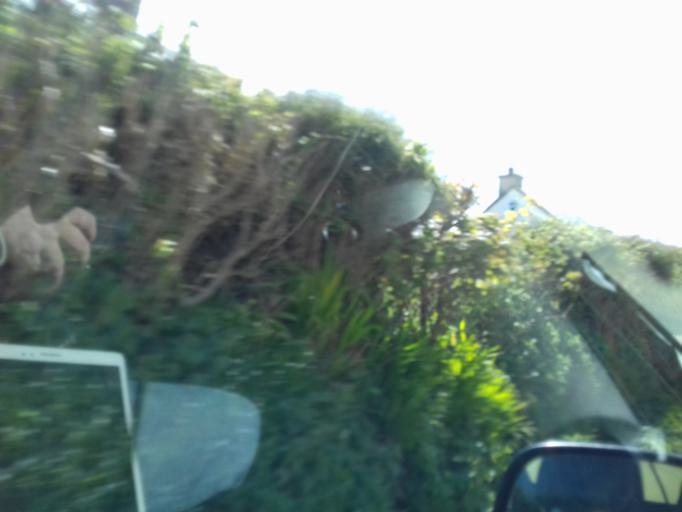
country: IE
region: Munster
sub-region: Waterford
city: Dunmore East
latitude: 52.2220
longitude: -6.8620
